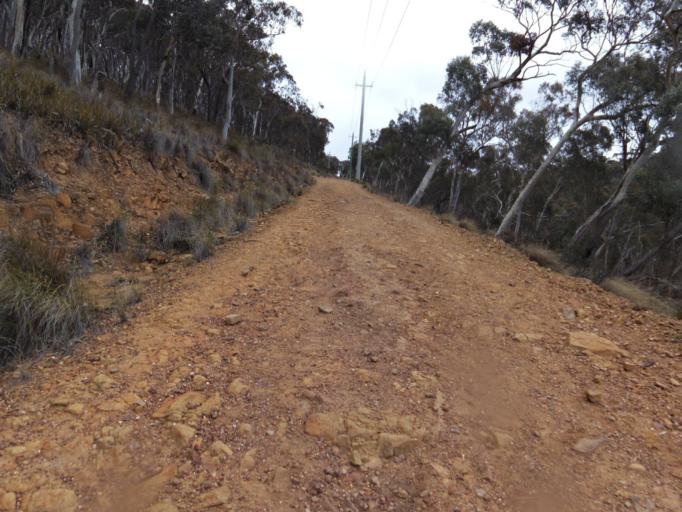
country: AU
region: Australian Capital Territory
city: Acton
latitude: -35.2693
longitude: 149.1014
